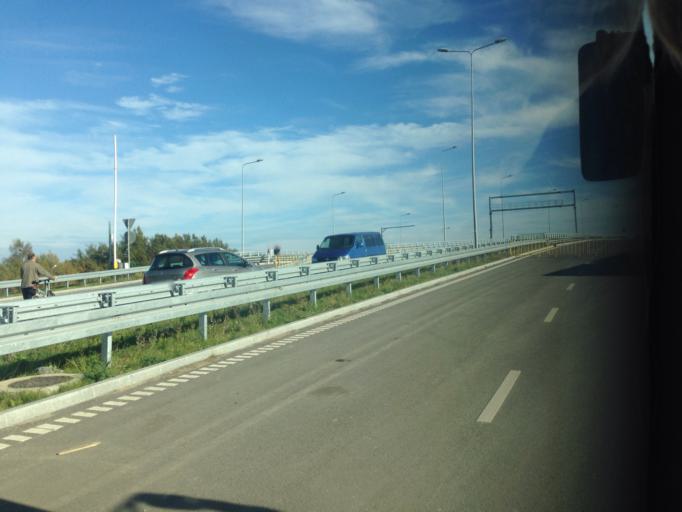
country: PL
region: Pomeranian Voivodeship
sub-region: Gdansk
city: Gdansk
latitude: 54.3790
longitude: 18.6755
